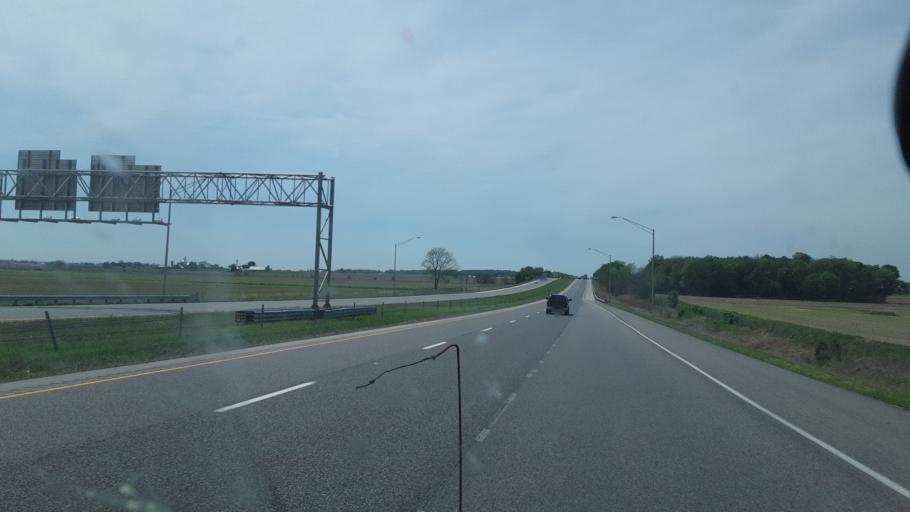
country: US
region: Indiana
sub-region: Gibson County
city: Haubstadt
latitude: 38.1673
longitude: -87.5563
